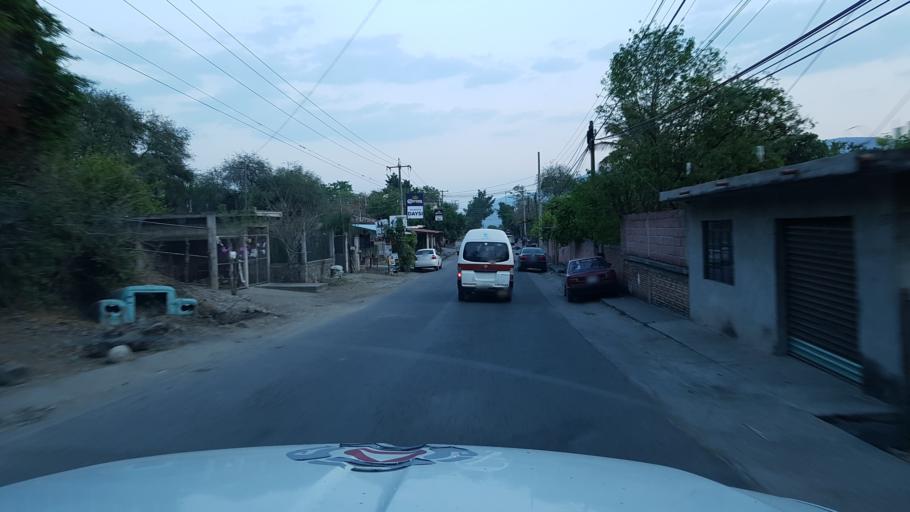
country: MX
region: Morelos
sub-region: Tlaltizapan de Zapata
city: Colonia Palo Prieto (Chipitongo)
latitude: 18.7017
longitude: -99.1060
